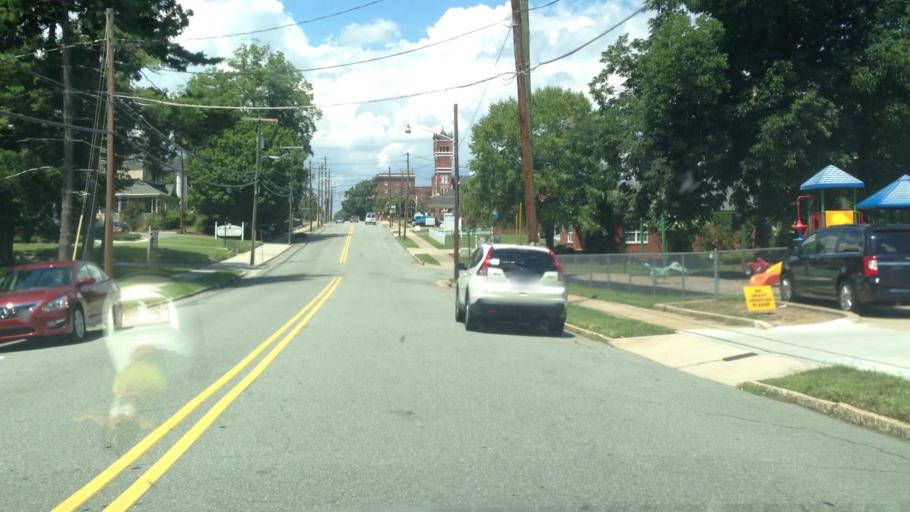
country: US
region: North Carolina
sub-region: Rockingham County
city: Reidsville
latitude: 36.3571
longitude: -79.6661
